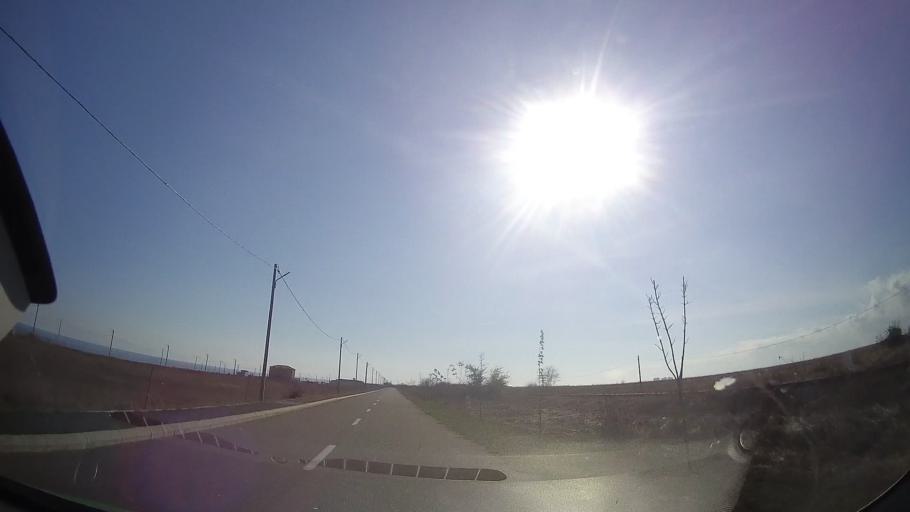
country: RO
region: Constanta
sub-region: Comuna Costinesti
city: Schitu
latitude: 43.9314
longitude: 28.6314
